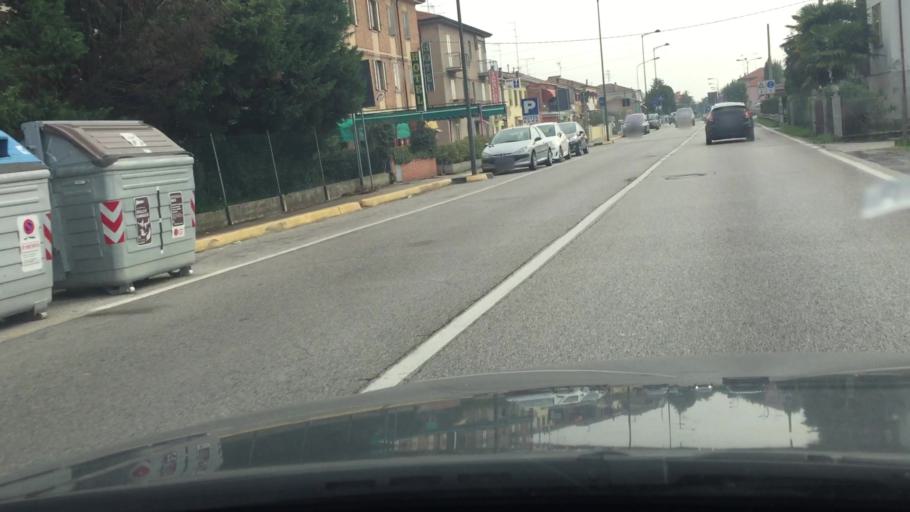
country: IT
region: Emilia-Romagna
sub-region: Provincia di Ferrara
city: Ferrara
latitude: 44.8413
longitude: 11.5854
